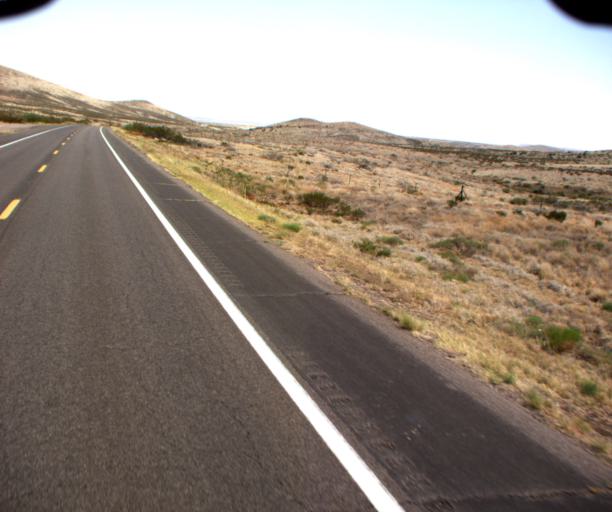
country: US
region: Arizona
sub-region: Greenlee County
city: Clifton
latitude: 32.7441
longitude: -109.2152
